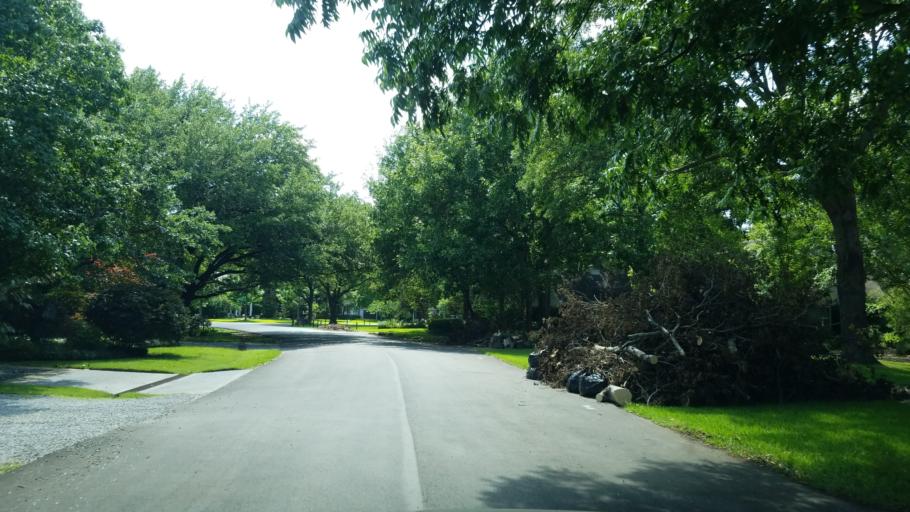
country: US
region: Texas
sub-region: Dallas County
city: University Park
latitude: 32.8846
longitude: -96.8349
